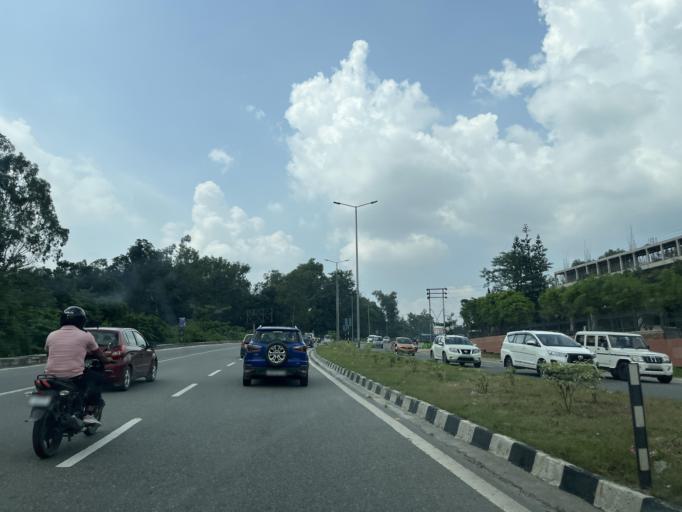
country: IN
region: Uttarakhand
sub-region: Dehradun
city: Raipur
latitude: 30.2663
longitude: 78.0815
